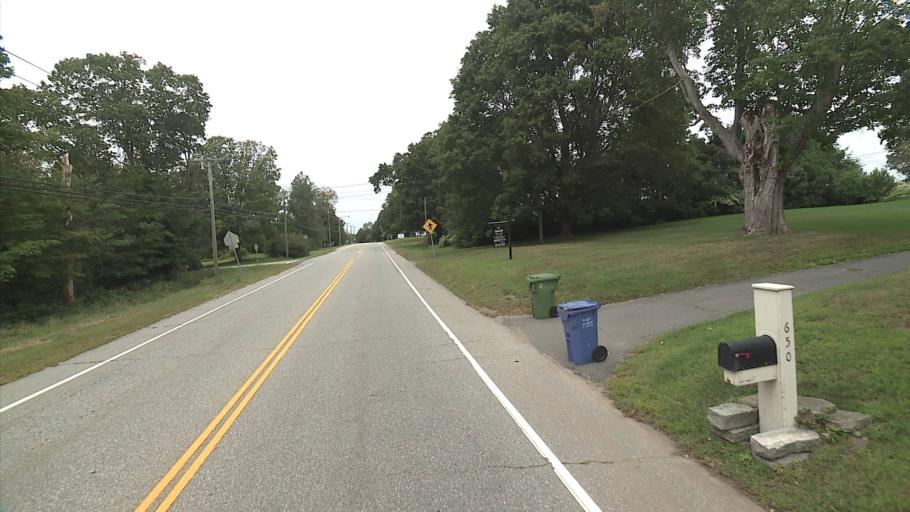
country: US
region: Connecticut
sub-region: Tolland County
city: Hebron
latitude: 41.6790
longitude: -72.4121
